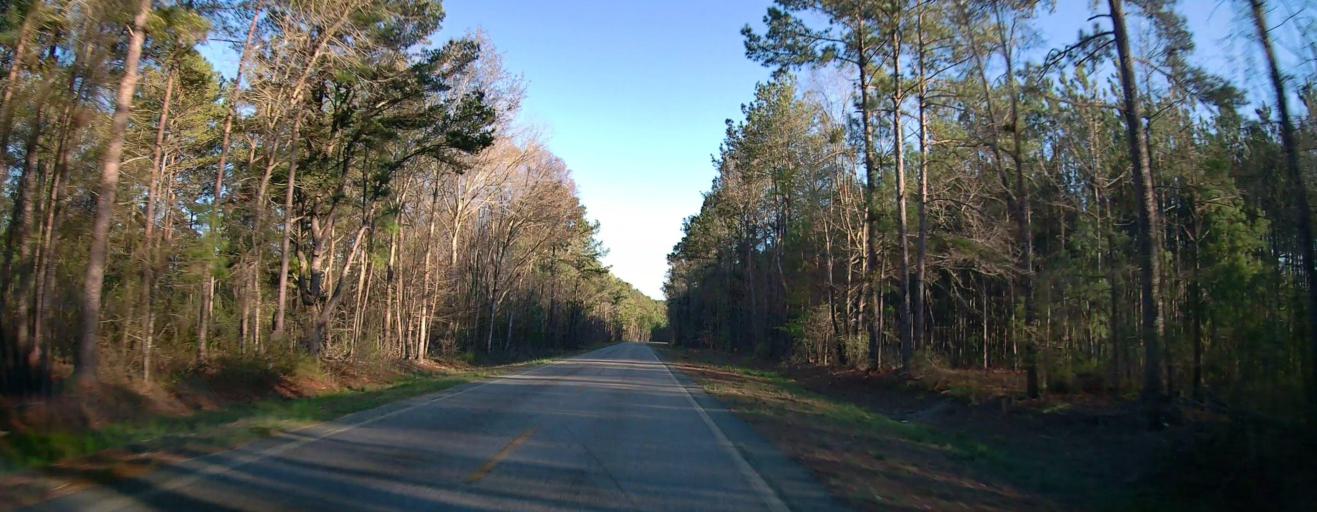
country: US
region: Georgia
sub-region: Wilcox County
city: Abbeville
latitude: 32.0903
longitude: -83.2951
